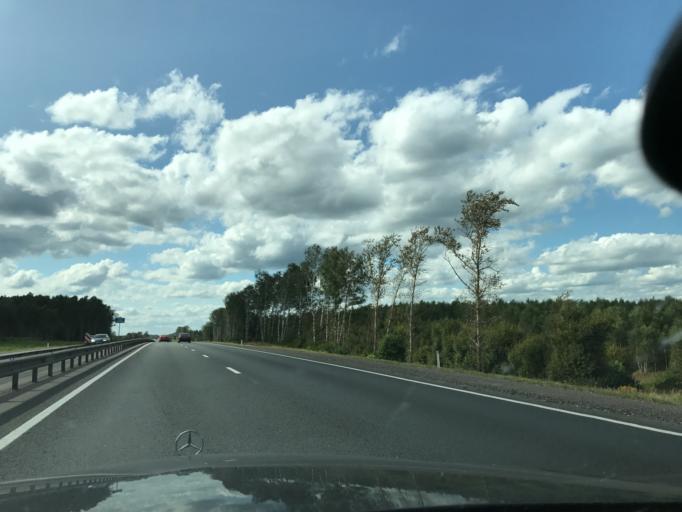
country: RU
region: Vladimir
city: Melekhovo
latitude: 56.2043
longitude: 41.1559
